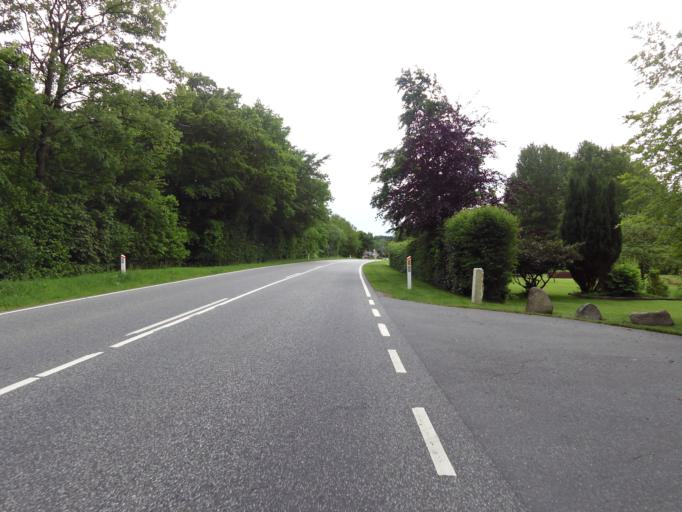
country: DK
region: South Denmark
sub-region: Haderslev Kommune
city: Gram
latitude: 55.3036
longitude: 9.0615
